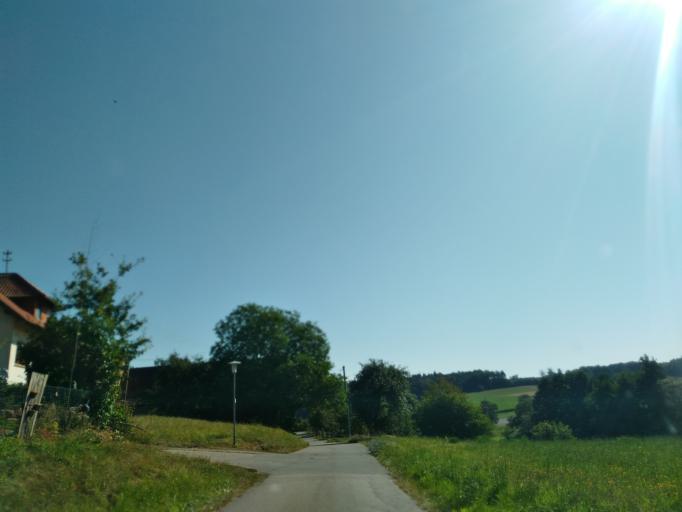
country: DE
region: Baden-Wuerttemberg
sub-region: Karlsruhe Region
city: Buchen
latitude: 49.5246
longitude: 9.2698
